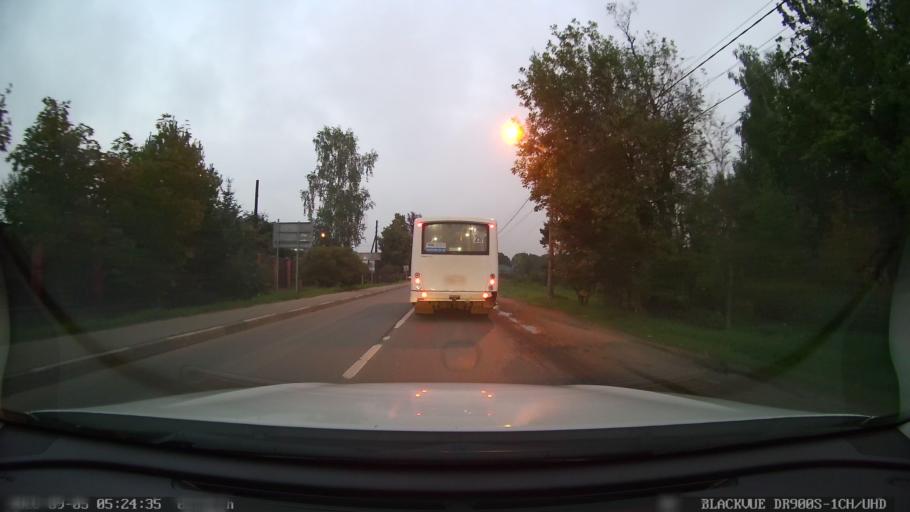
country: RU
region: Moskovskaya
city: Levoberezhnaya
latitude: 55.9196
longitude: 37.4687
